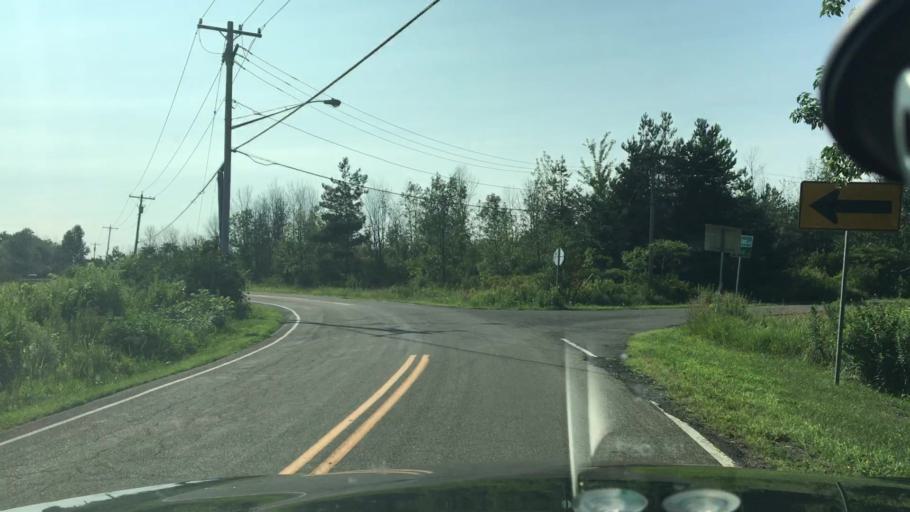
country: US
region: New York
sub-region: Erie County
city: Angola
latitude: 42.6295
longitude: -78.9802
